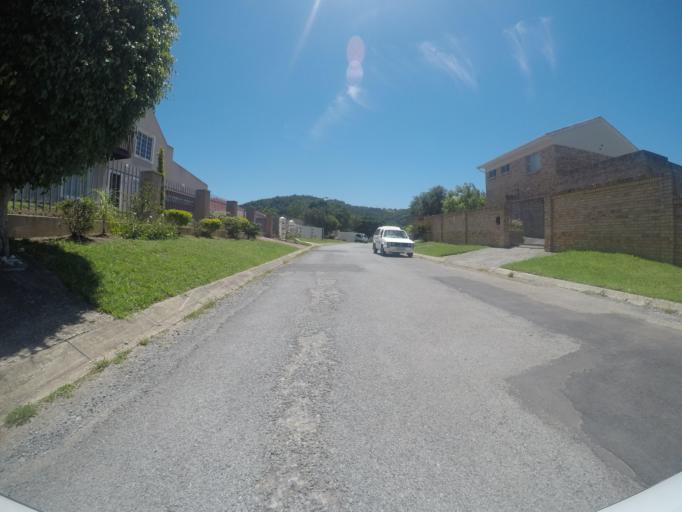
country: ZA
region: Eastern Cape
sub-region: Buffalo City Metropolitan Municipality
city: East London
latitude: -32.9288
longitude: 27.9966
